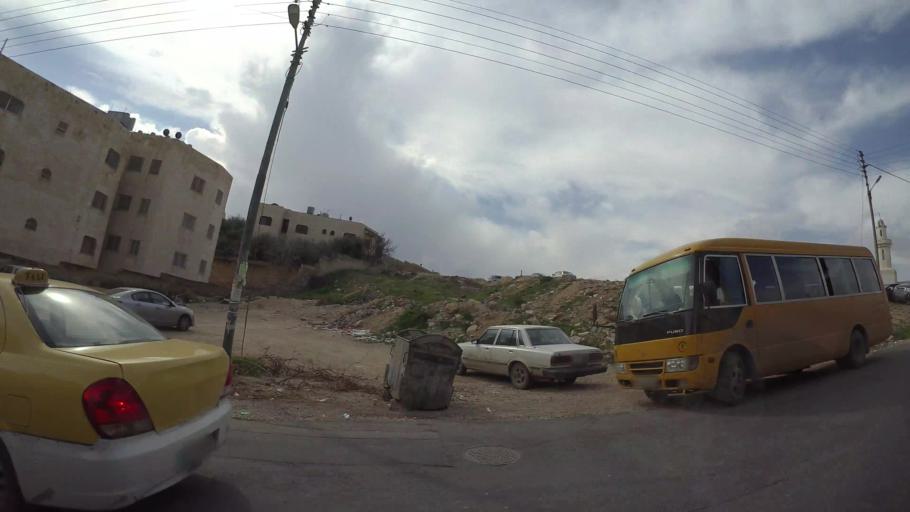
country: JO
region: Amman
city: Amman
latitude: 32.0106
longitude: 35.9363
